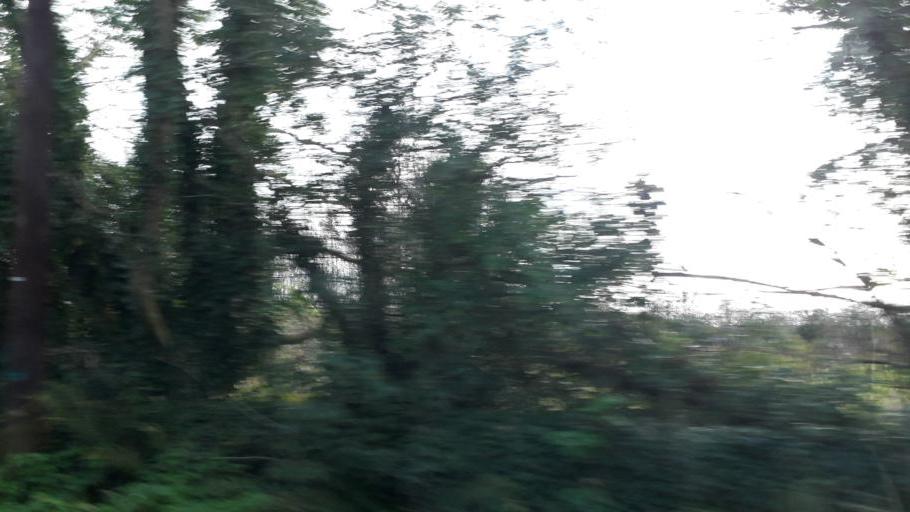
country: IE
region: Leinster
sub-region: Fingal County
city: Skerries
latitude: 53.5696
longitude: -6.1288
